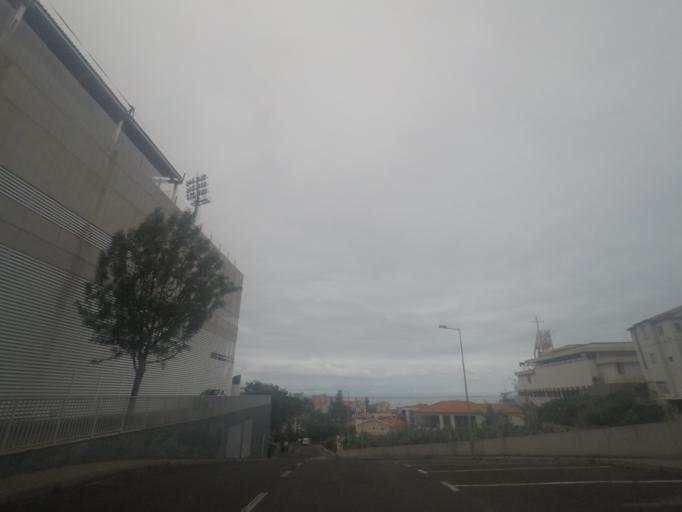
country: PT
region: Madeira
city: Camara de Lobos
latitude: 32.6548
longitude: -16.9829
